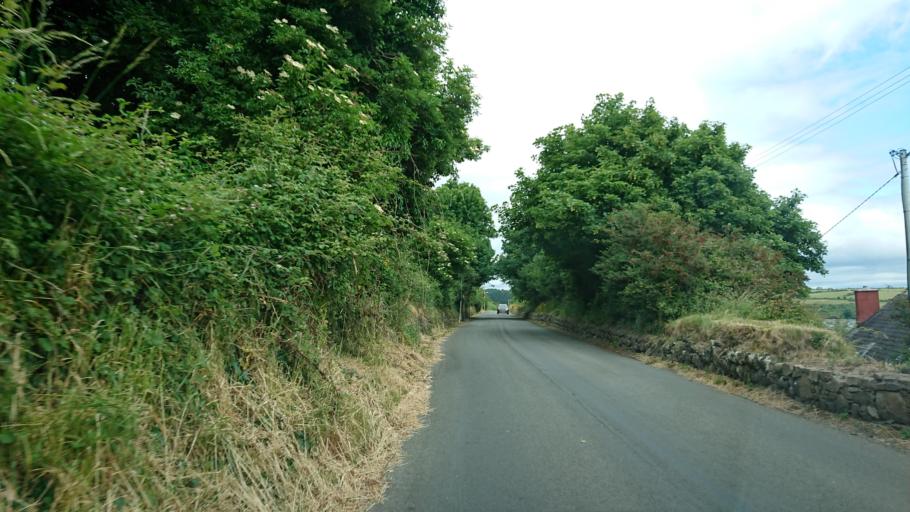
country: IE
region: Munster
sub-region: Waterford
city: Dunmore East
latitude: 52.2333
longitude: -6.9720
